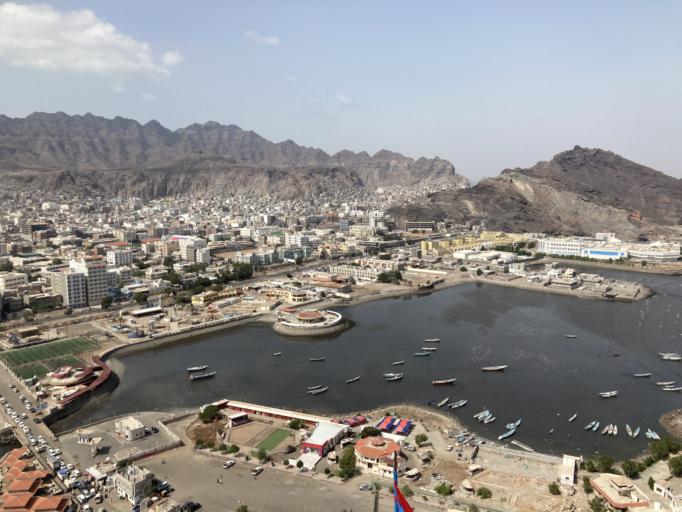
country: YE
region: Aden
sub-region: Craiter
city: Aden
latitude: 12.7789
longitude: 45.0495
